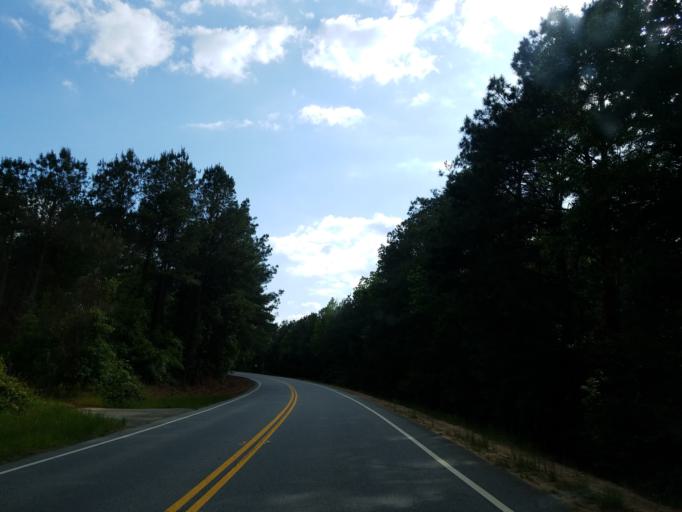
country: US
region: Georgia
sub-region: Crisp County
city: Cordele
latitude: 32.0040
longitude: -83.7426
